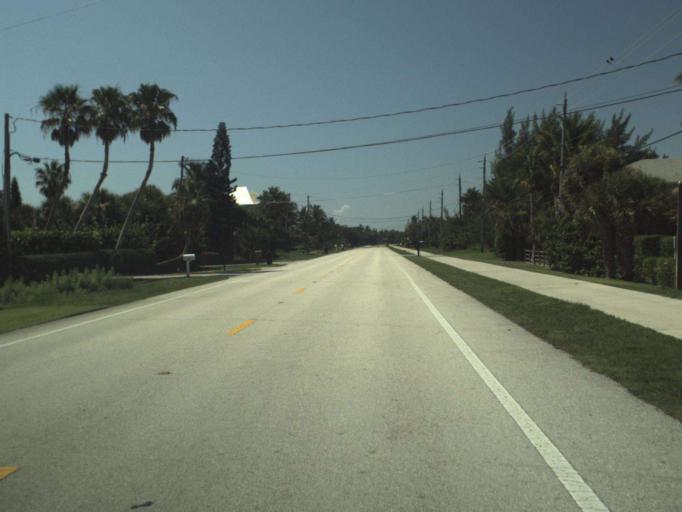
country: US
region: Florida
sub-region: Indian River County
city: Sebastian
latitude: 27.8281
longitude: -80.4316
